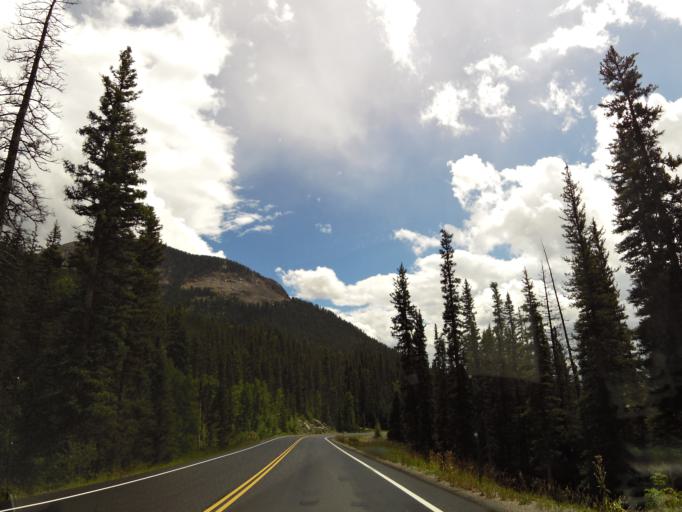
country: US
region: Colorado
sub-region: San Juan County
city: Silverton
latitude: 37.6829
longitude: -107.7793
